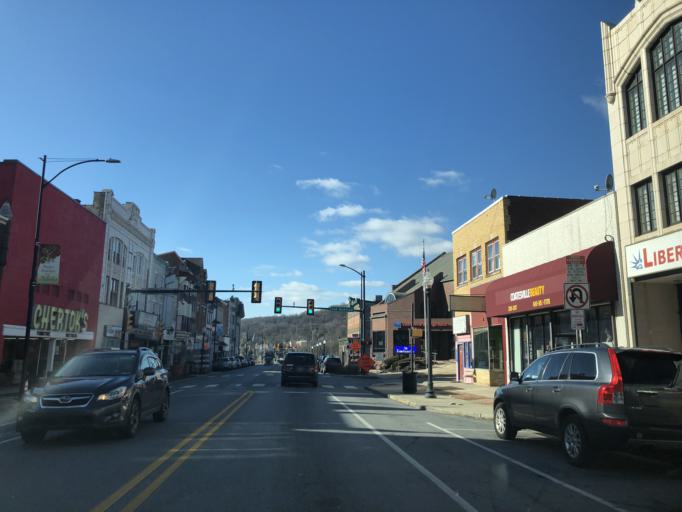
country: US
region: Pennsylvania
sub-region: Chester County
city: Coatesville
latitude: 39.9835
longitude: -75.8215
